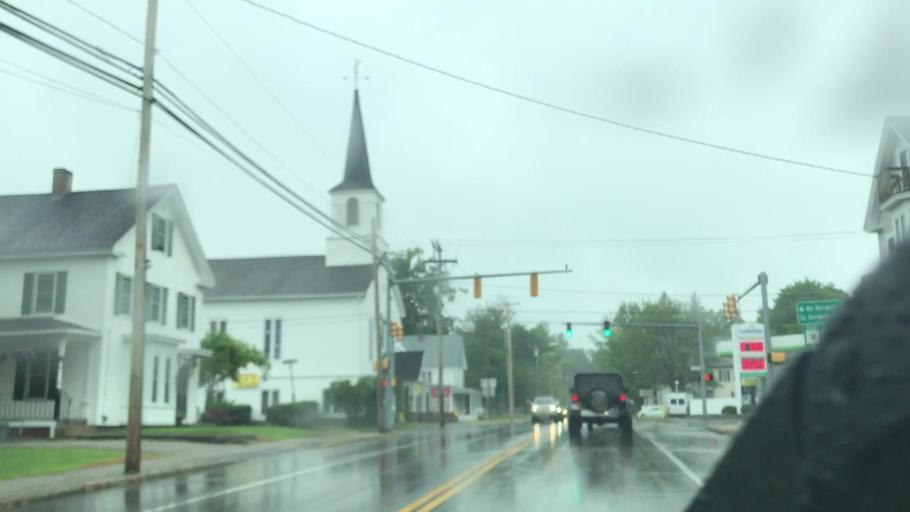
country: US
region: Maine
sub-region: York County
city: Berwick
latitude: 43.2675
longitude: -70.8621
